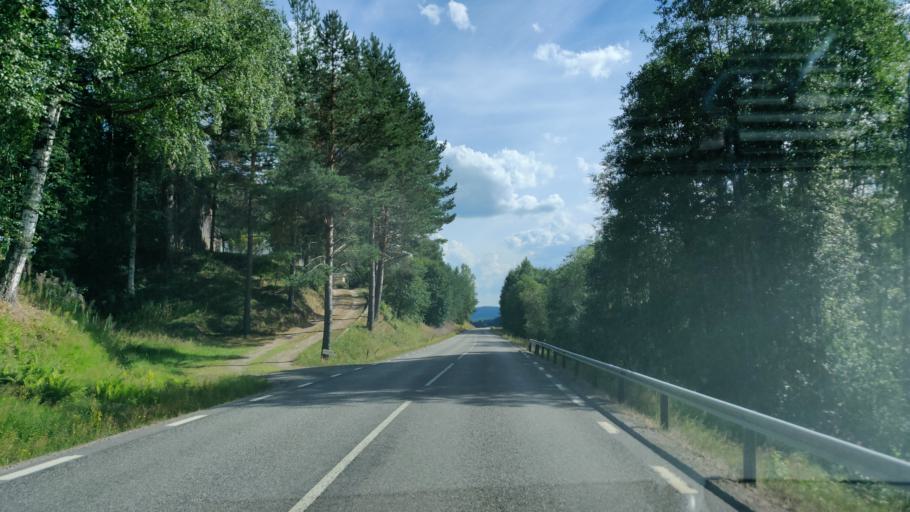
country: SE
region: Vaermland
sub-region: Hagfors Kommun
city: Ekshaerad
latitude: 60.1734
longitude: 13.5295
